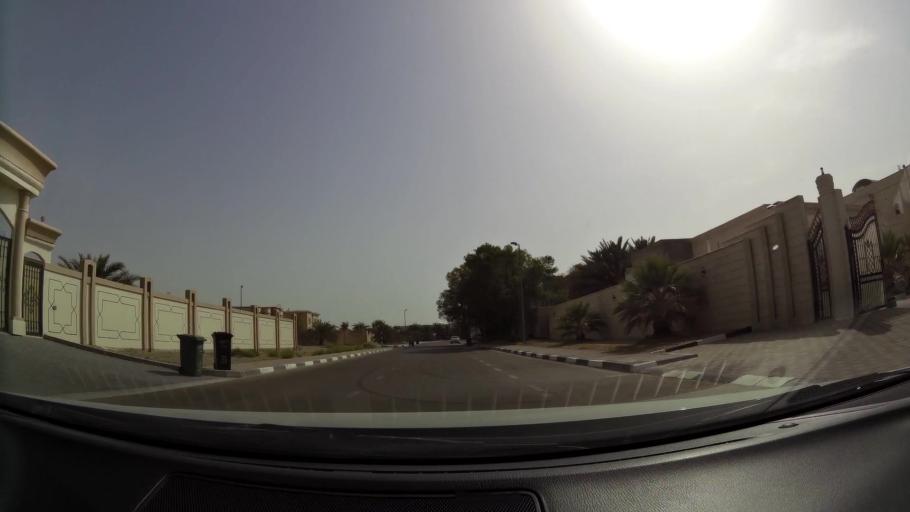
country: AE
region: Abu Dhabi
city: Al Ain
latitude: 24.1507
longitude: 55.7037
